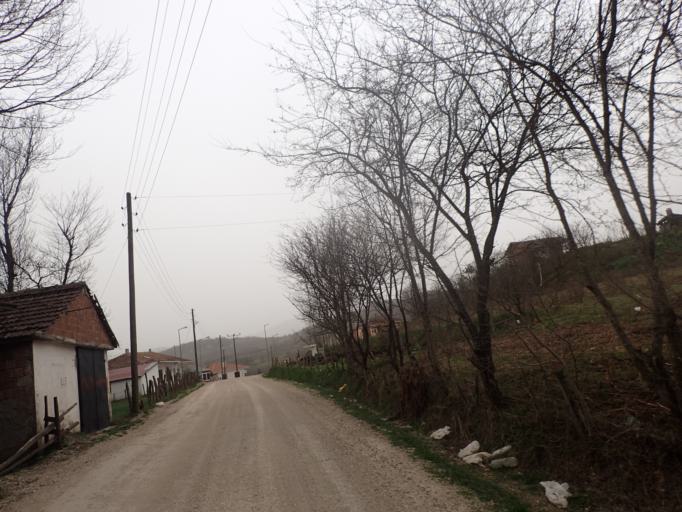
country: TR
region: Ordu
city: Kumru
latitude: 40.8223
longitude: 37.1861
